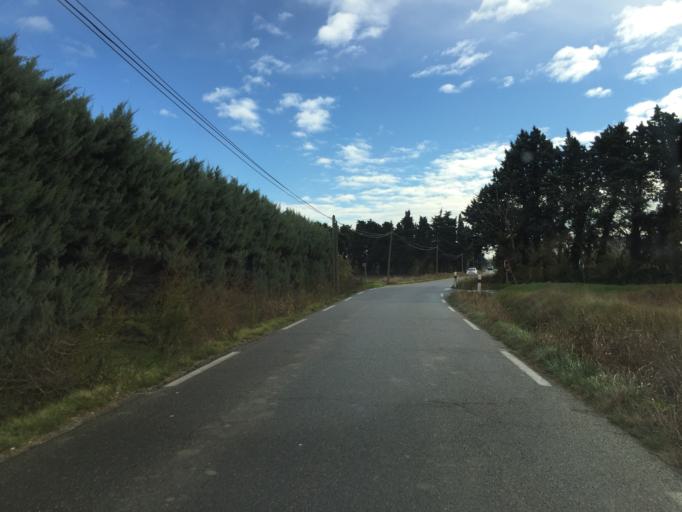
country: FR
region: Provence-Alpes-Cote d'Azur
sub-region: Departement du Vaucluse
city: Althen-des-Paluds
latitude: 43.9721
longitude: 4.9781
